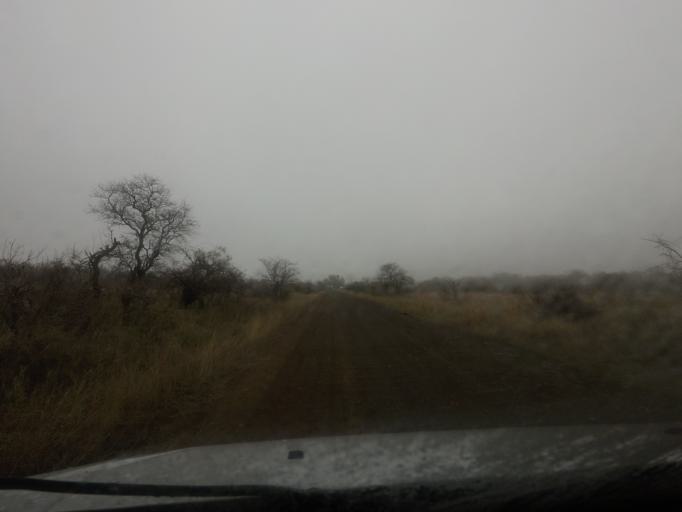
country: ZA
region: Limpopo
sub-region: Mopani District Municipality
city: Phalaborwa
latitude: -24.2622
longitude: 31.6469
